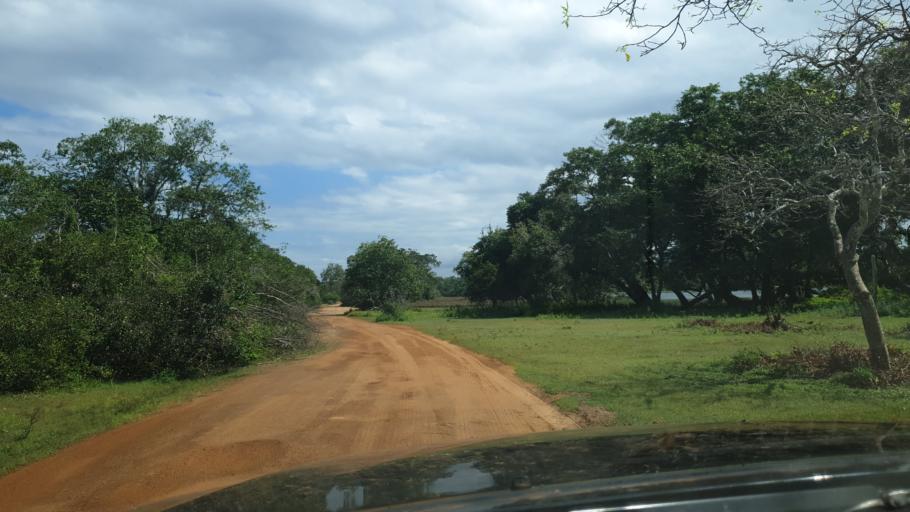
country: LK
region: North Central
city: Anuradhapura
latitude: 8.4221
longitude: 80.0067
